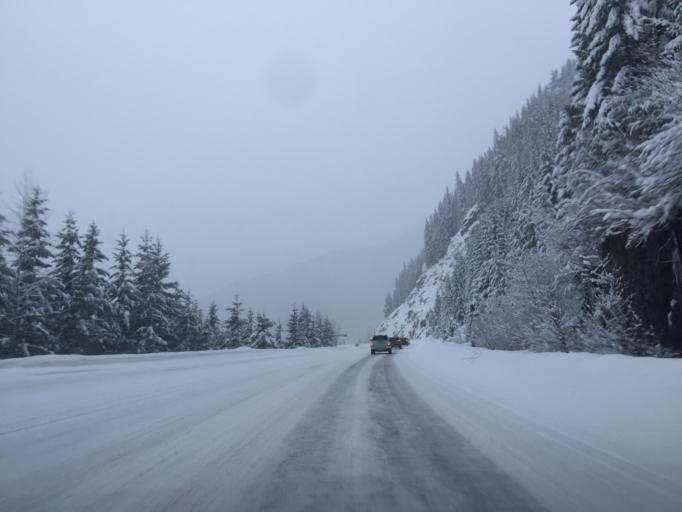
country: US
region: Washington
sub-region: Chelan County
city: Leavenworth
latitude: 47.7200
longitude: -121.1293
